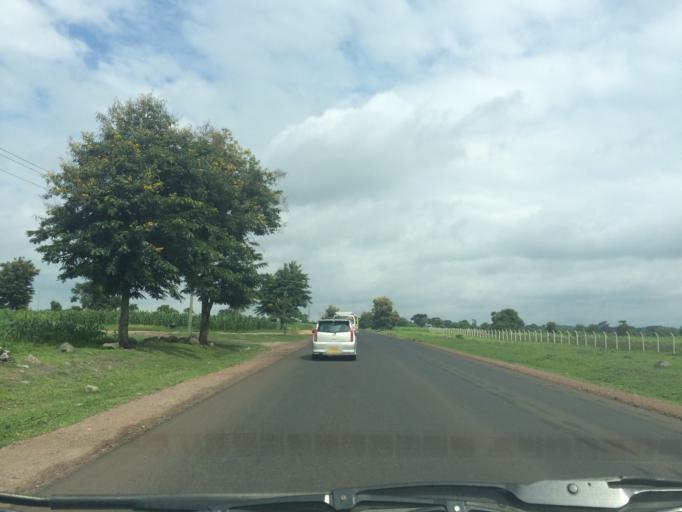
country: TZ
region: Arusha
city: Kingori
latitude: -3.3879
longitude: 36.9567
